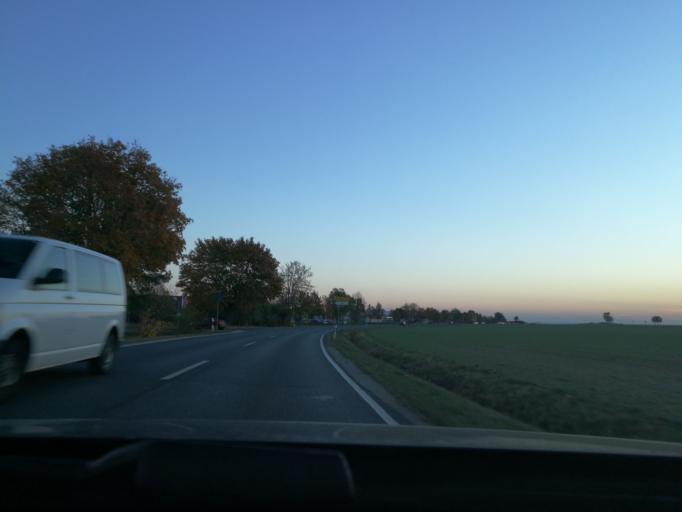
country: DE
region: Bavaria
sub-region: Regierungsbezirk Mittelfranken
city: Obermichelbach
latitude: 49.5227
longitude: 10.9043
